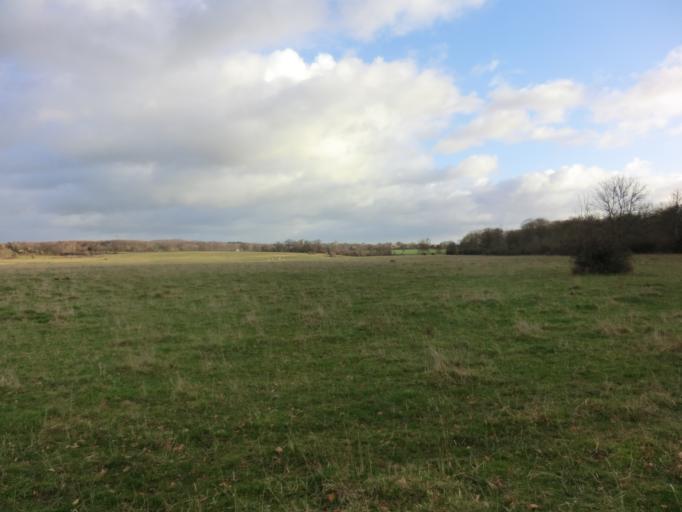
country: SE
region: Skane
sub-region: Lunds Kommun
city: Genarp
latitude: 55.6795
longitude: 13.3295
